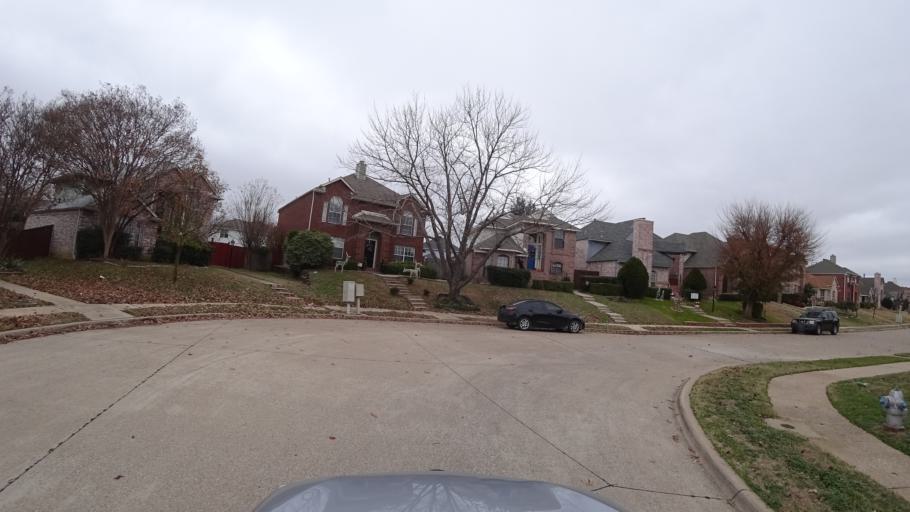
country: US
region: Texas
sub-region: Denton County
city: Lewisville
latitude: 33.0240
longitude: -97.0290
